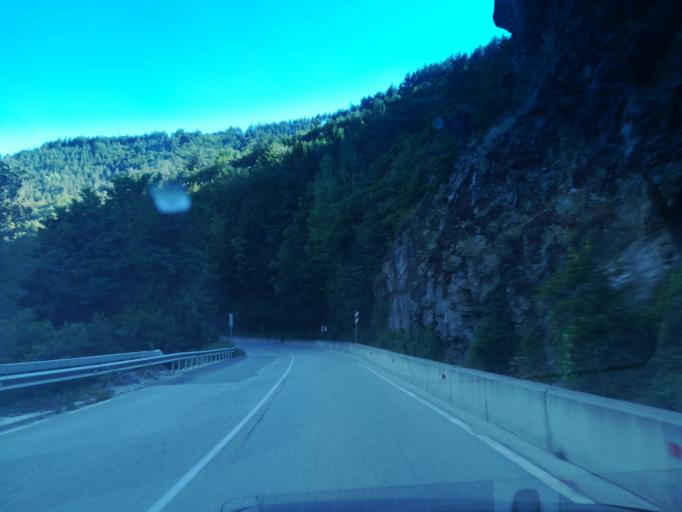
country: BG
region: Smolyan
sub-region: Obshtina Chepelare
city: Chepelare
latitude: 41.8246
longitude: 24.6916
